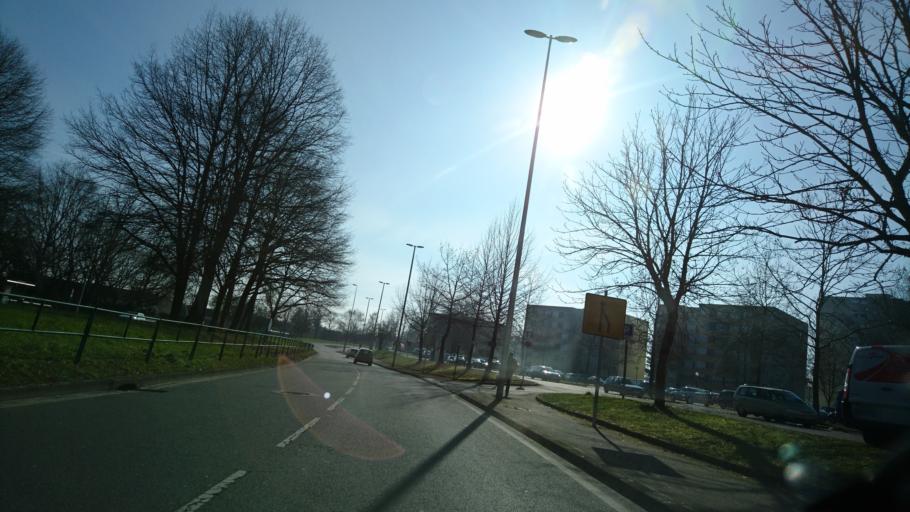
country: FR
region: Limousin
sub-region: Departement de la Haute-Vienne
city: Rilhac-Rancon
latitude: 45.8790
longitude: 1.2984
